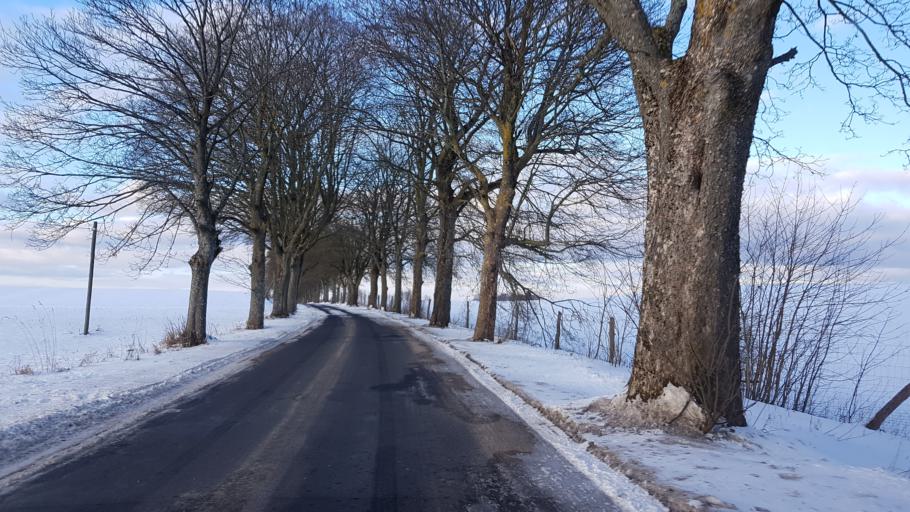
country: PL
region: West Pomeranian Voivodeship
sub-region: Powiat koszalinski
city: Bobolice
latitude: 53.9801
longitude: 16.6910
